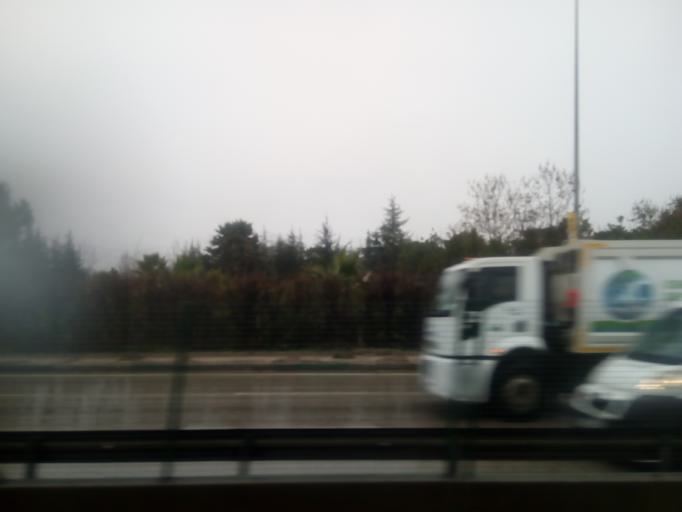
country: TR
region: Bursa
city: Yildirim
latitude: 40.2109
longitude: 29.0235
